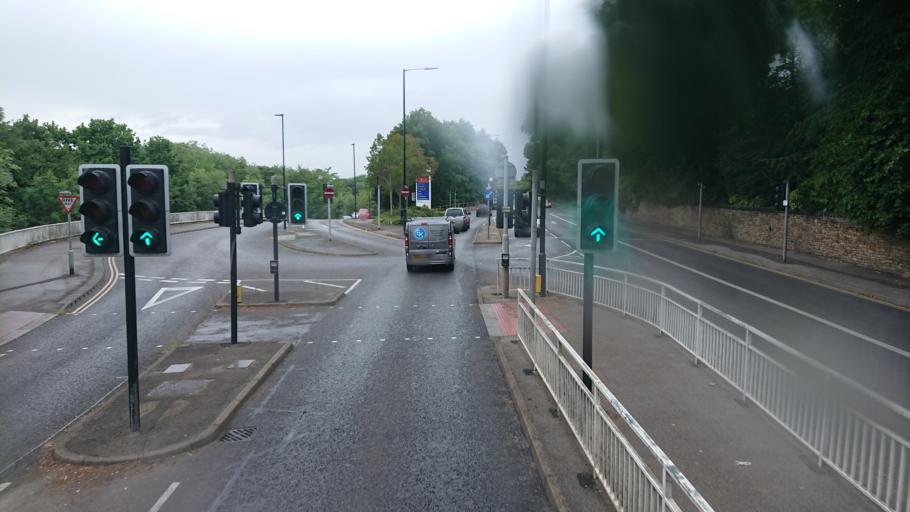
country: GB
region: England
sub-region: Sheffield
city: Sheffield
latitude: 53.3499
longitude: -1.4902
